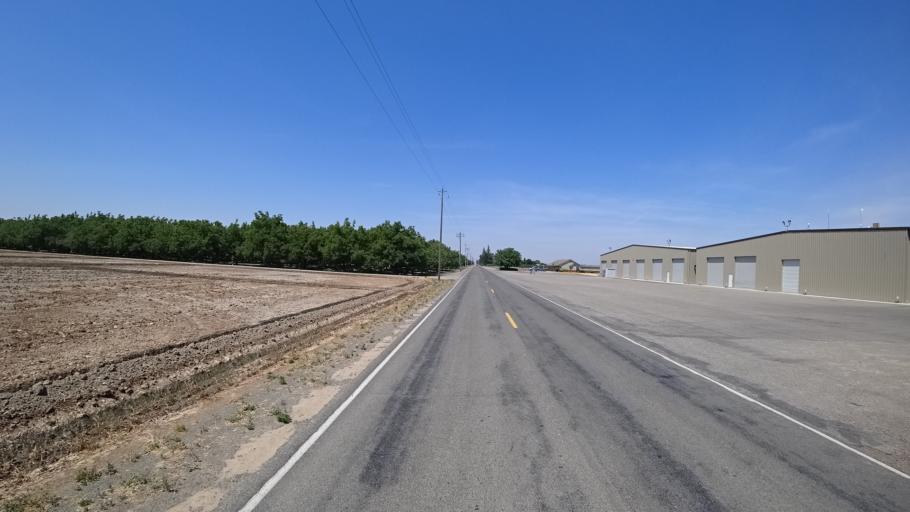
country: US
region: California
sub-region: Kings County
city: Lucerne
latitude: 36.4012
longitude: -119.6222
